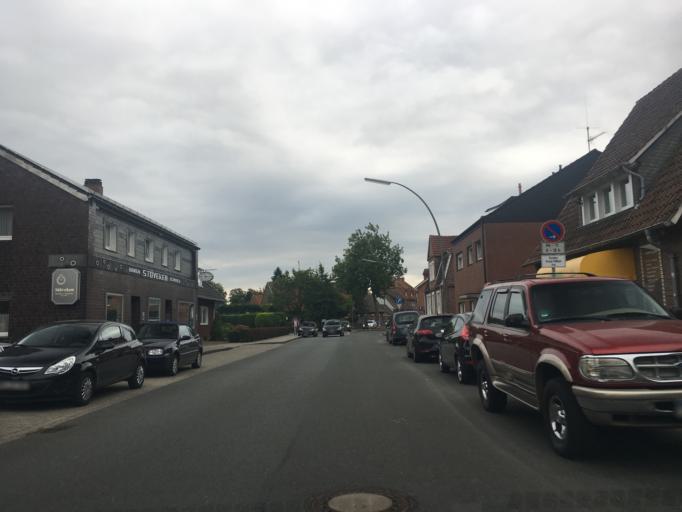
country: DE
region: North Rhine-Westphalia
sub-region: Regierungsbezirk Munster
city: Muenster
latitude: 51.9562
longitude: 7.5328
